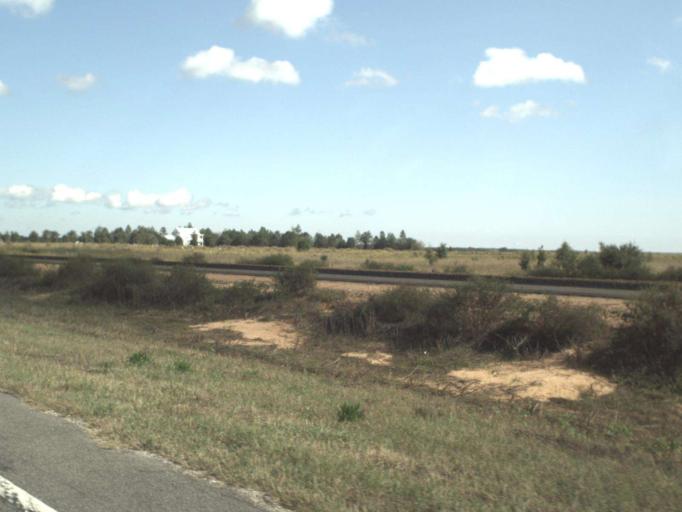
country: US
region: Florida
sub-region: Walton County
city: Freeport
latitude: 30.5525
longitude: -86.1064
